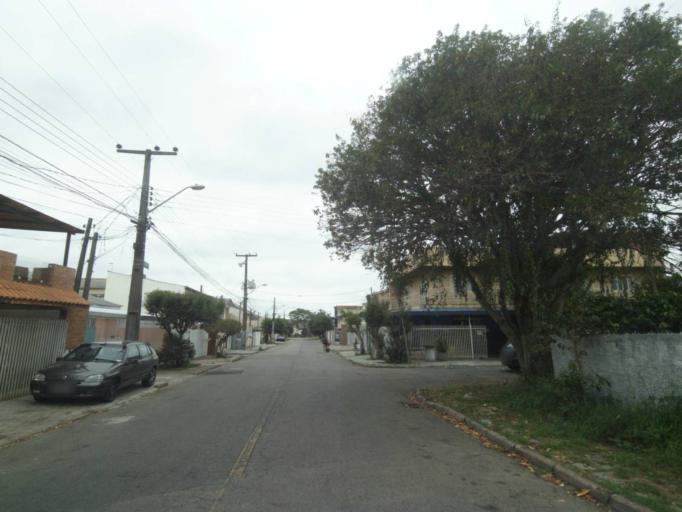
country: BR
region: Parana
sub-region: Sao Jose Dos Pinhais
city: Sao Jose dos Pinhais
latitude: -25.5374
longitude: -49.2636
